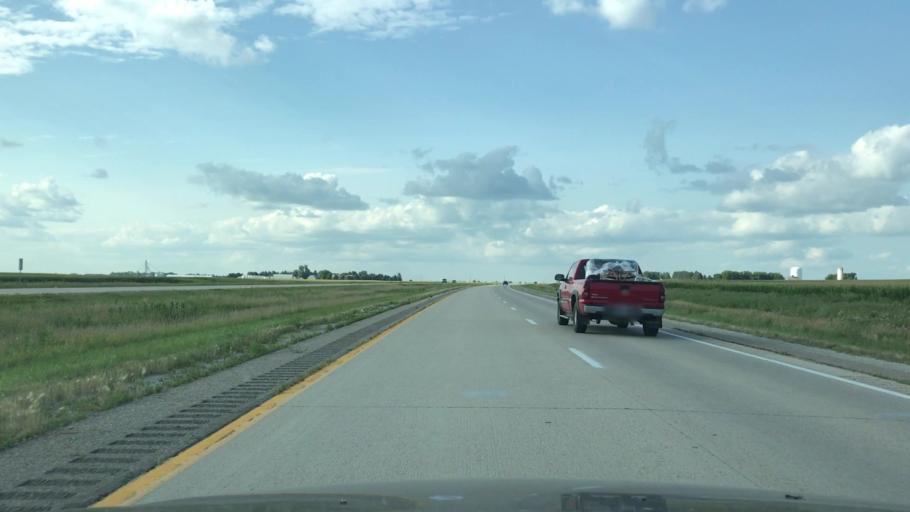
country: US
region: Iowa
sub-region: Osceola County
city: Sibley
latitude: 43.4527
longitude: -95.7133
